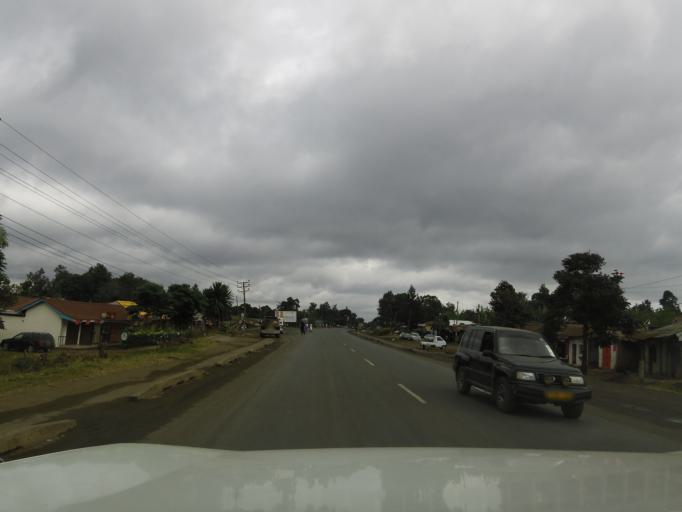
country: TZ
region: Arusha
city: Arusha
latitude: -3.3673
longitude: 36.7151
